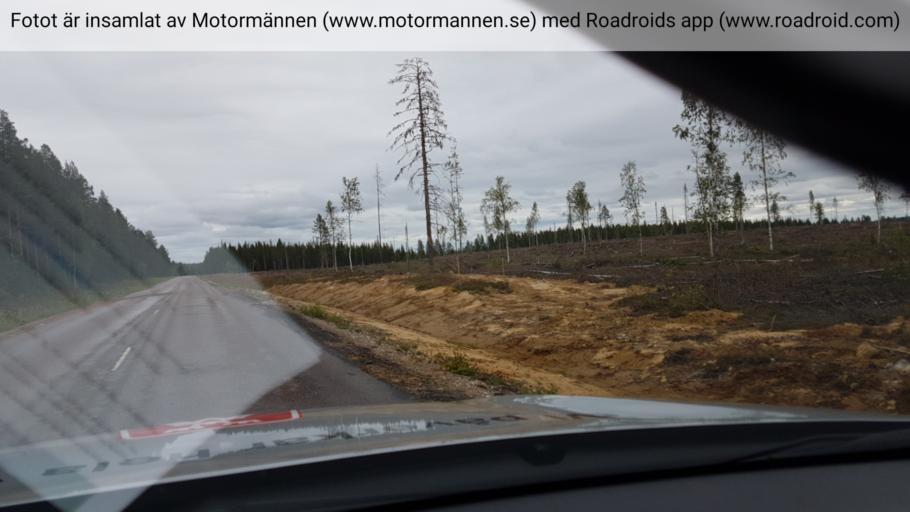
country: SE
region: Norrbotten
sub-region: Overkalix Kommun
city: OEverkalix
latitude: 67.0630
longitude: 22.2734
